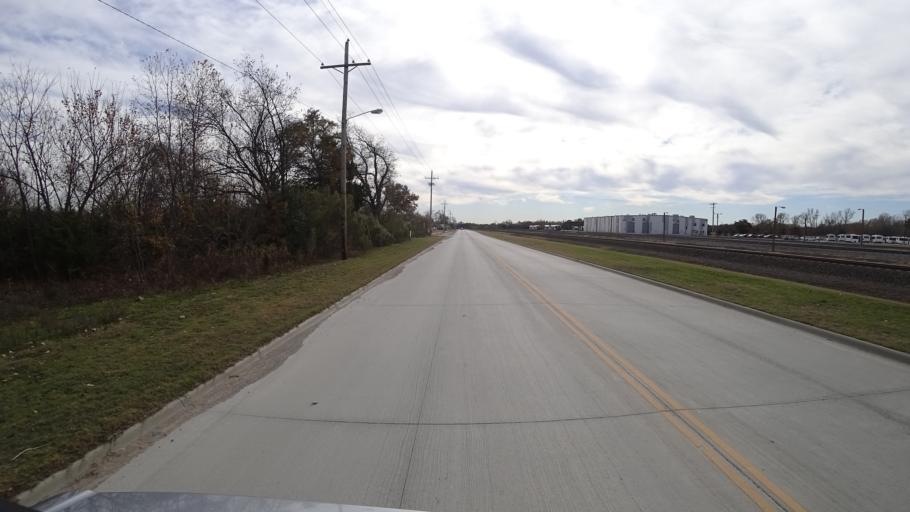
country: US
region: Texas
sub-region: Denton County
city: Lewisville
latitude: 33.0376
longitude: -96.9810
